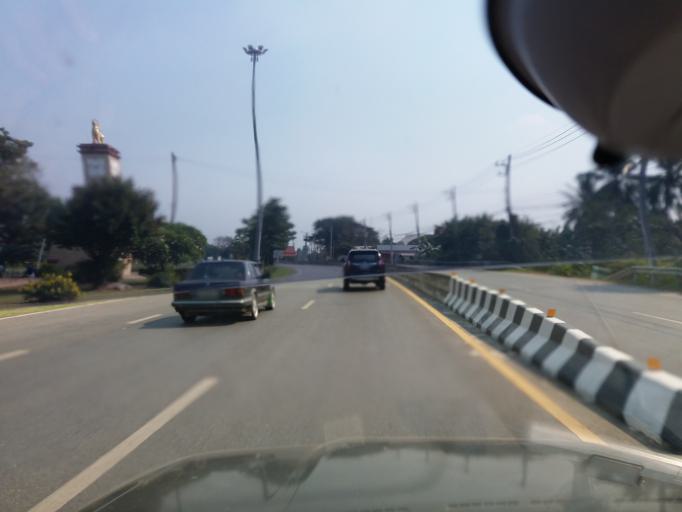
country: TH
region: Sing Buri
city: Bang Racham
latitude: 14.8842
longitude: 100.3237
